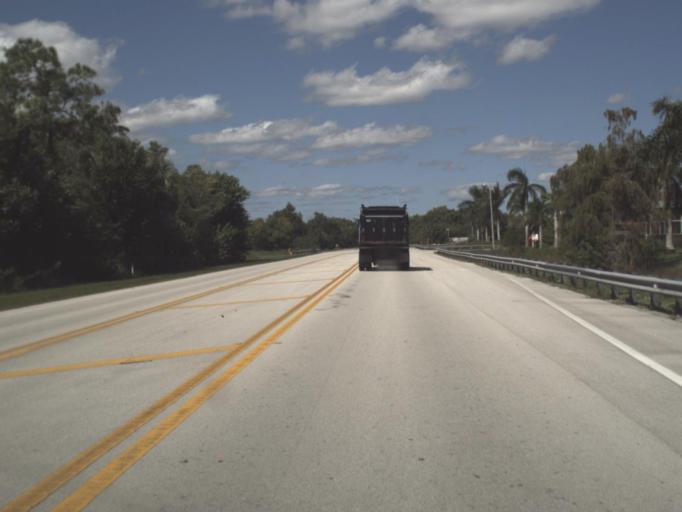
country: US
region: Florida
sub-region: Collier County
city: Lely Resort
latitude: 26.0245
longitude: -81.6385
